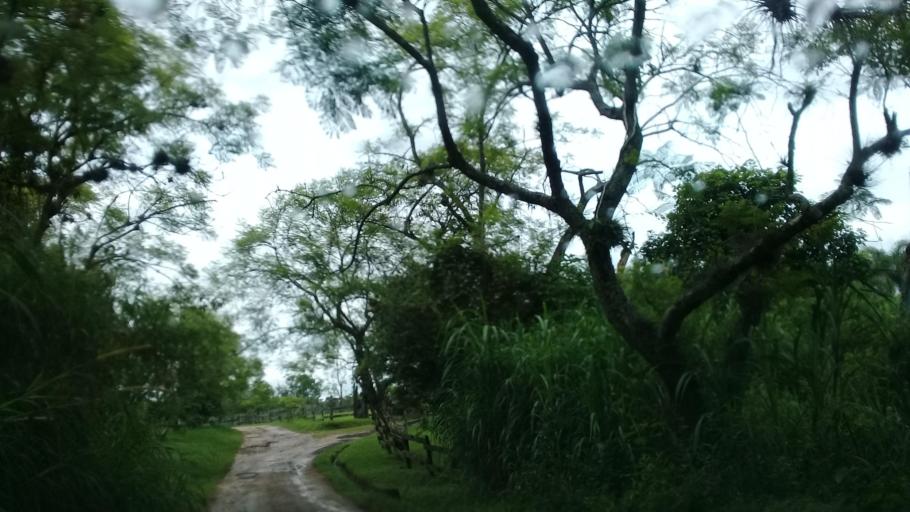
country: MX
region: Veracruz
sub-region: Emiliano Zapata
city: Jacarandas
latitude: 19.5072
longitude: -96.8433
